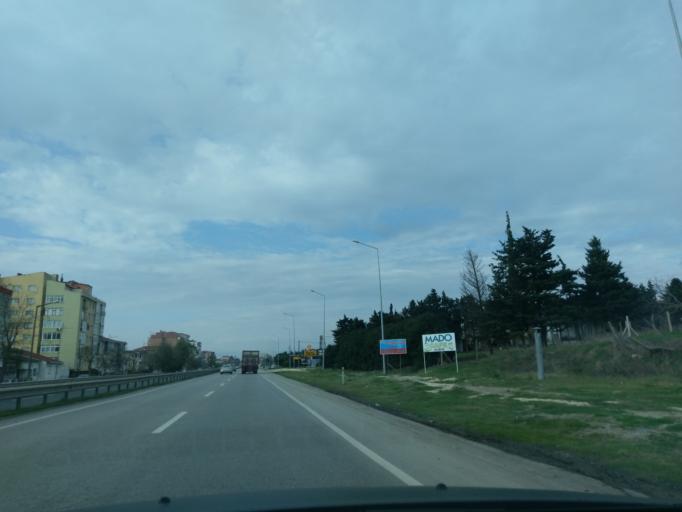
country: TR
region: Istanbul
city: Celaliye
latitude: 41.0461
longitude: 28.4062
